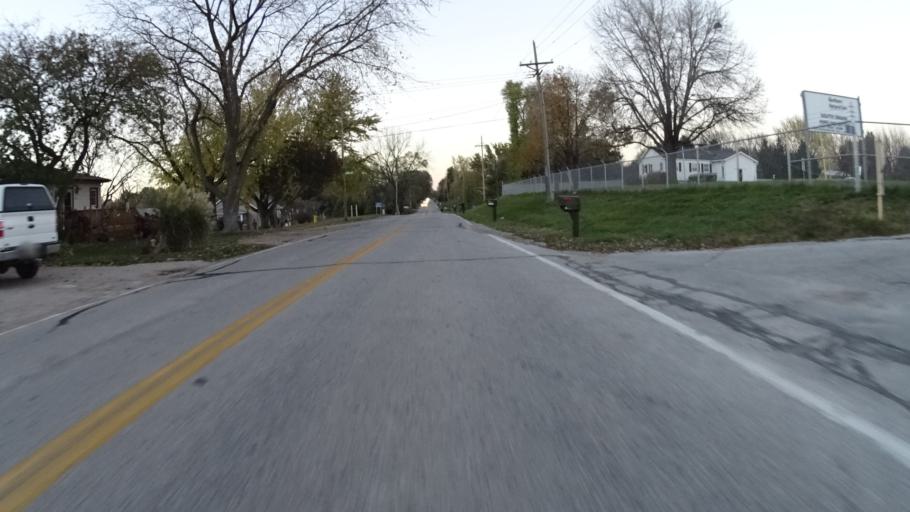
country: US
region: Nebraska
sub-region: Sarpy County
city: Offutt Air Force Base
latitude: 41.1759
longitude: -95.9527
